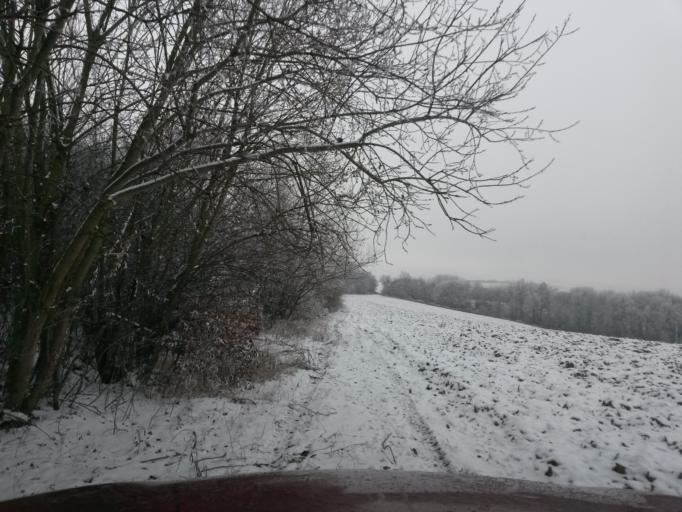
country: SK
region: Presovsky
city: Sabinov
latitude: 48.9808
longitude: 21.0828
